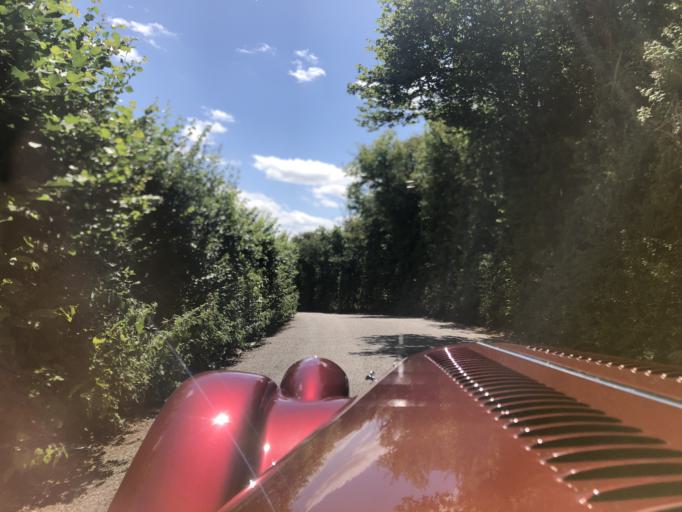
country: GB
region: England
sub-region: Kent
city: Shoreham
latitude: 51.3146
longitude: 0.1622
